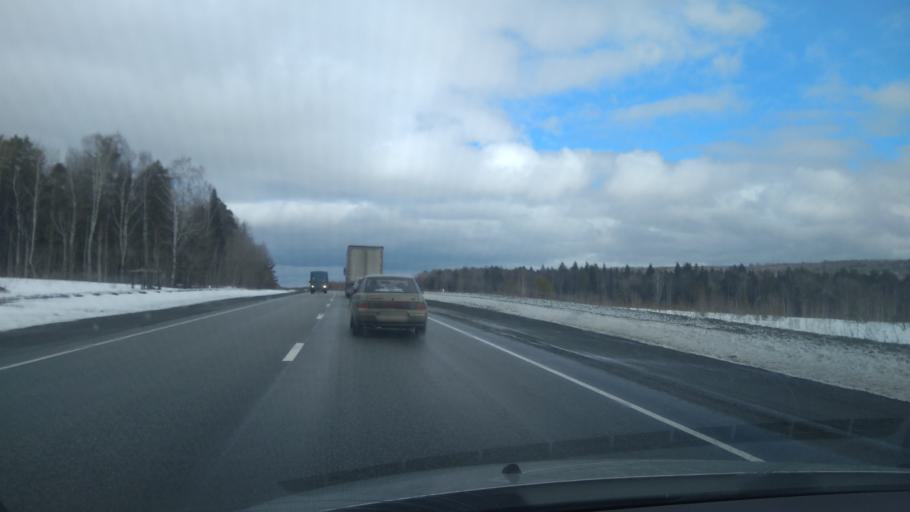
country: RU
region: Sverdlovsk
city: Bisert'
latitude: 56.8126
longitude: 58.7399
